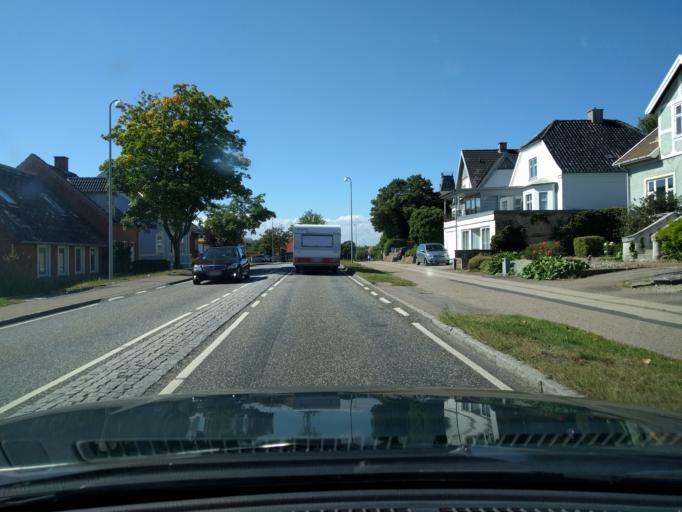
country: DK
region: Zealand
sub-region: Slagelse Kommune
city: Korsor
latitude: 55.3251
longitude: 11.1504
